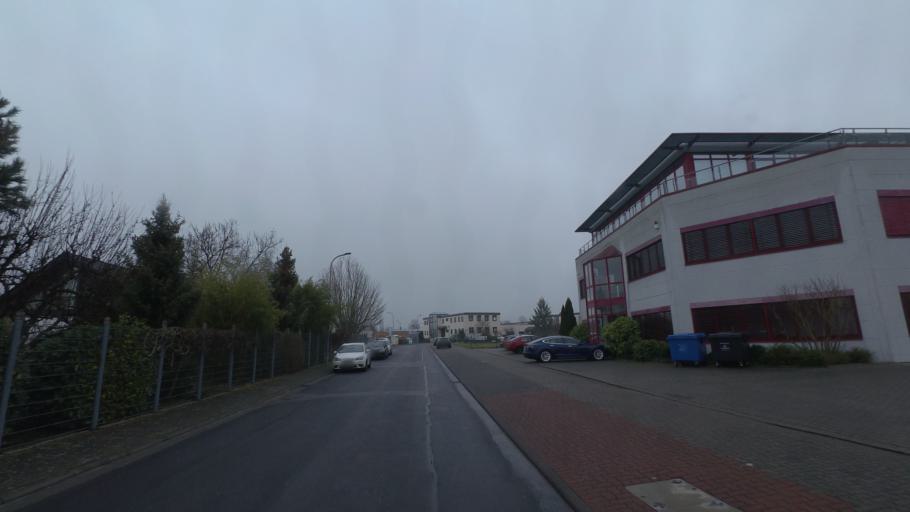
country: DE
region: Hesse
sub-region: Regierungsbezirk Darmstadt
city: Seligenstadt
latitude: 50.0646
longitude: 8.9679
